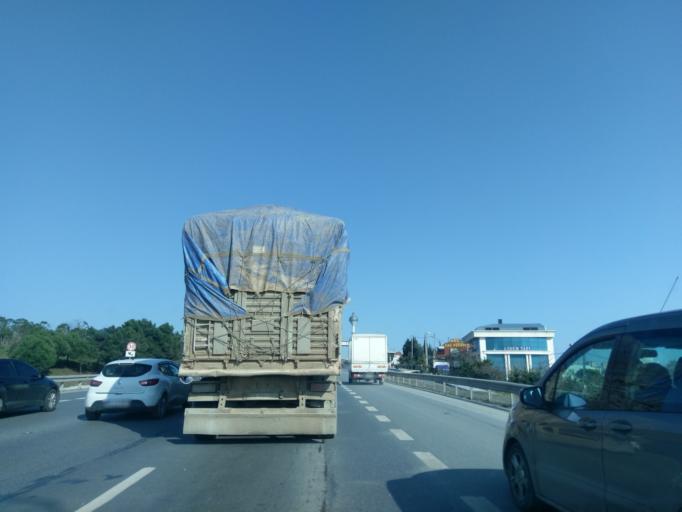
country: TR
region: Istanbul
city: Bueyuekcekmece
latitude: 41.0239
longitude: 28.6005
